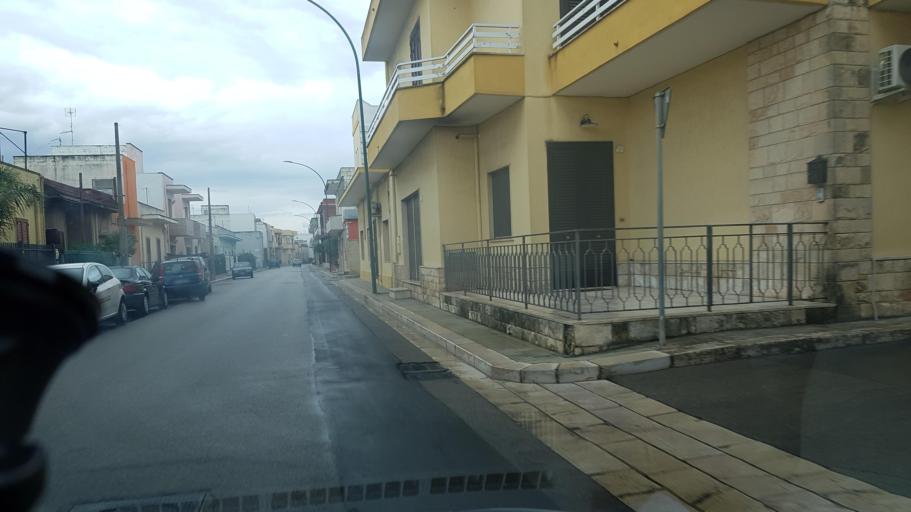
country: IT
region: Apulia
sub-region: Provincia di Lecce
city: Guagnano
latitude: 40.3970
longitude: 17.9535
